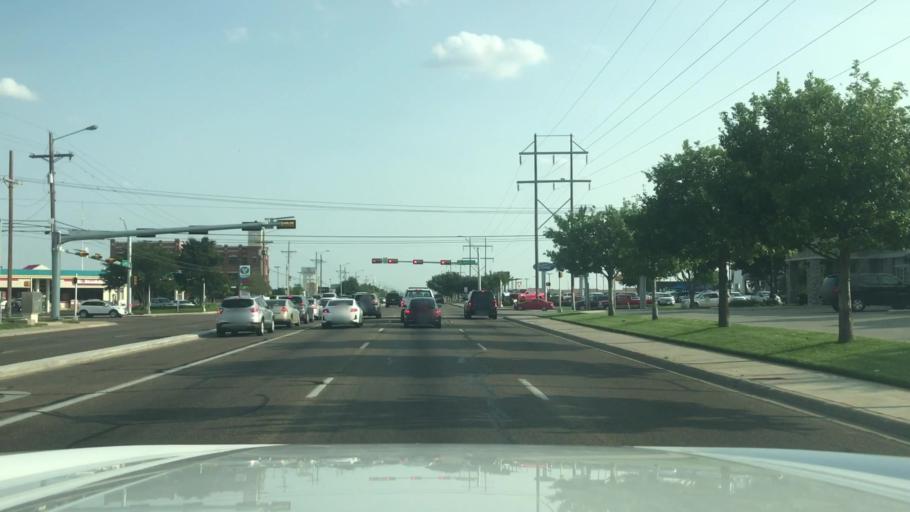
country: US
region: Texas
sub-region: Potter County
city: Amarillo
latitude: 35.1773
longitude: -101.9383
